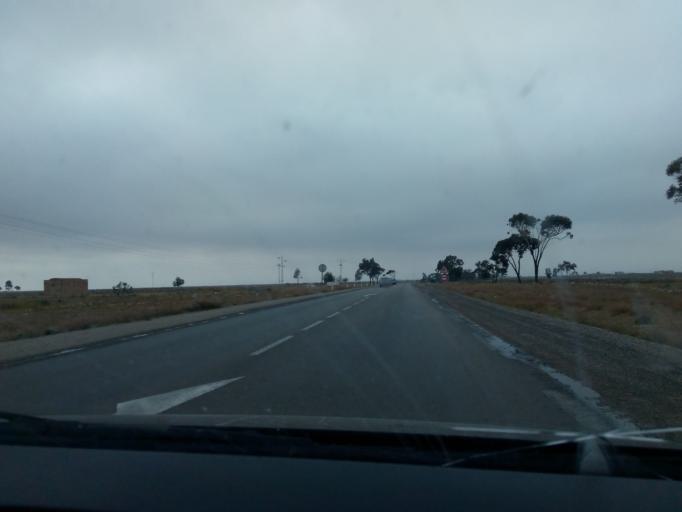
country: TN
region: Madanin
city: Medenine
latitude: 33.2738
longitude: 10.4684
